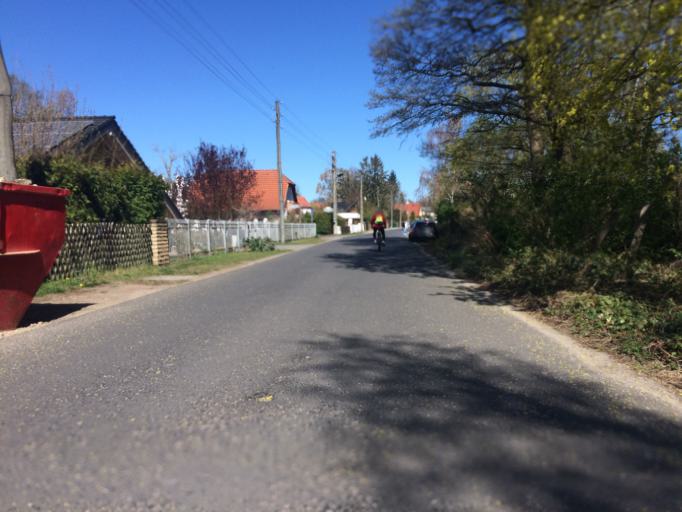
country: DE
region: Berlin
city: Rahnsdorf
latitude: 52.4295
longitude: 13.7129
